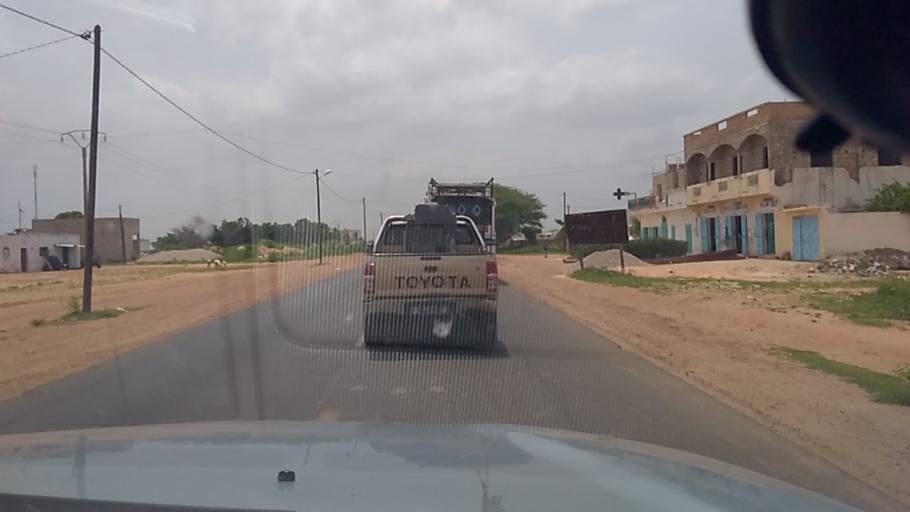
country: SN
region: Thies
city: Mekhe
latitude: 15.0112
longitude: -16.7416
